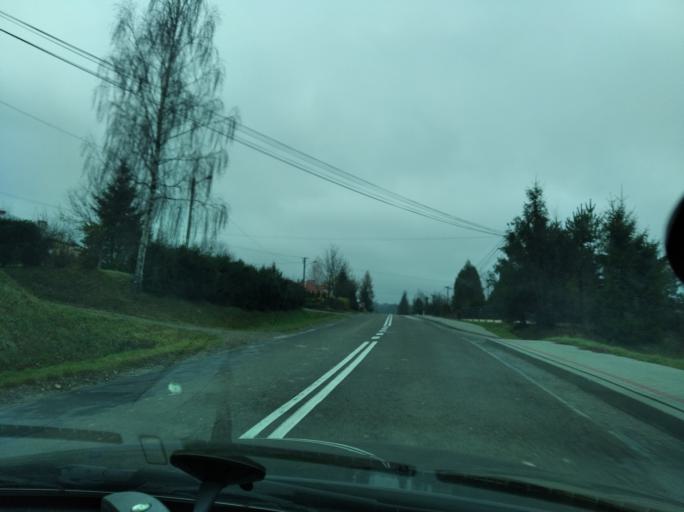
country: PL
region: Subcarpathian Voivodeship
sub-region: Powiat przeworski
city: Jawornik Polski
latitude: 49.8716
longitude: 22.2461
